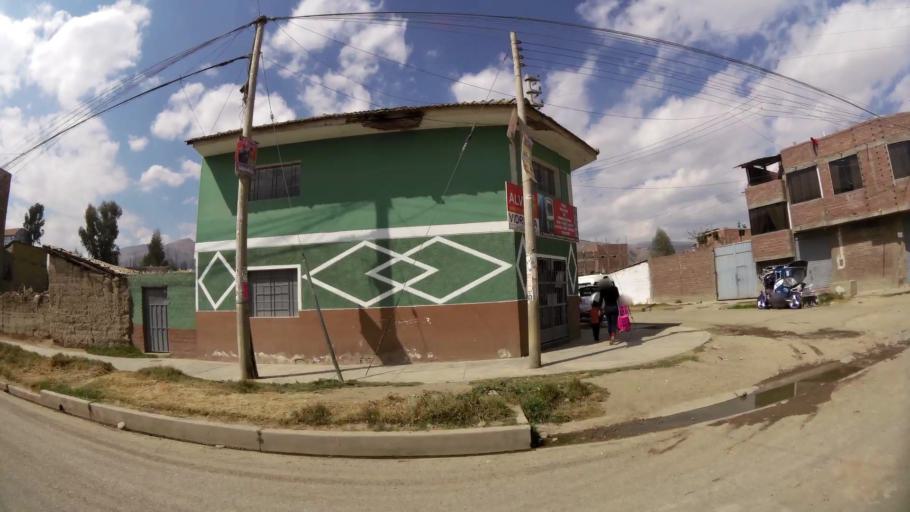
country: PE
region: Junin
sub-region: Provincia de Huancayo
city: Huancayo
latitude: -12.0912
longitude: -75.2066
